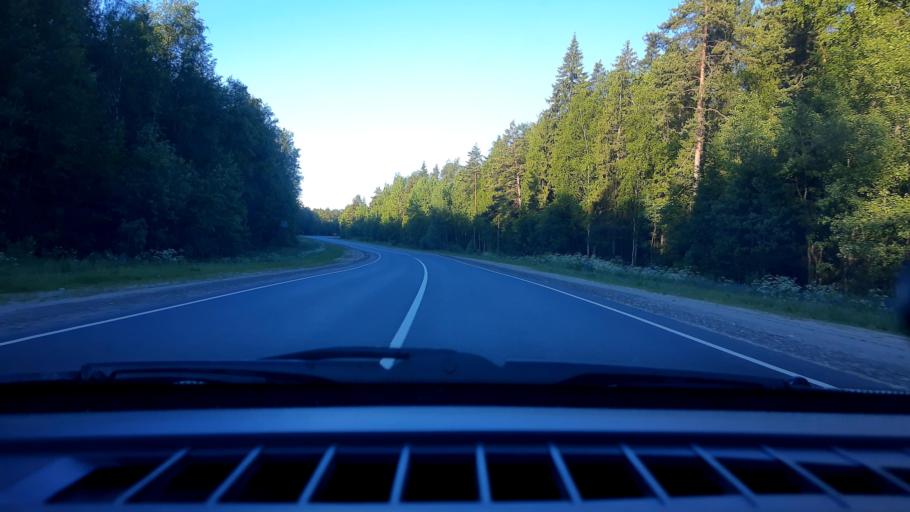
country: RU
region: Nizjnij Novgorod
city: Linda
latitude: 56.6406
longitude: 44.1079
